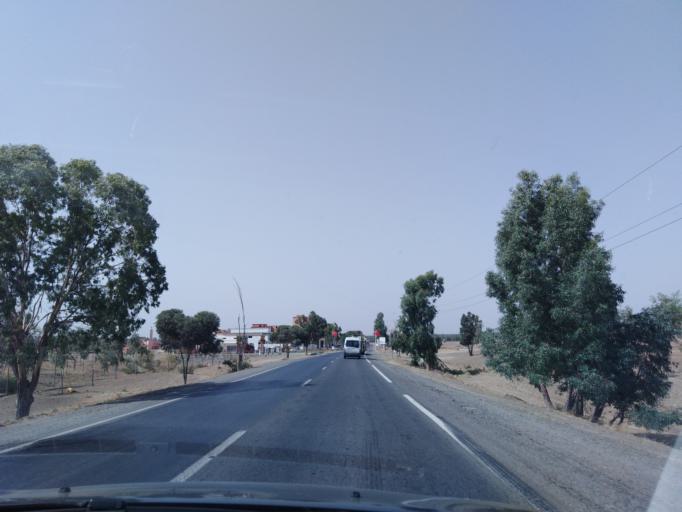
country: MA
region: Marrakech-Tensift-Al Haouz
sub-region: Kelaa-Des-Sraghna
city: Sidi Bou Othmane
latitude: 31.8894
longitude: -7.9439
